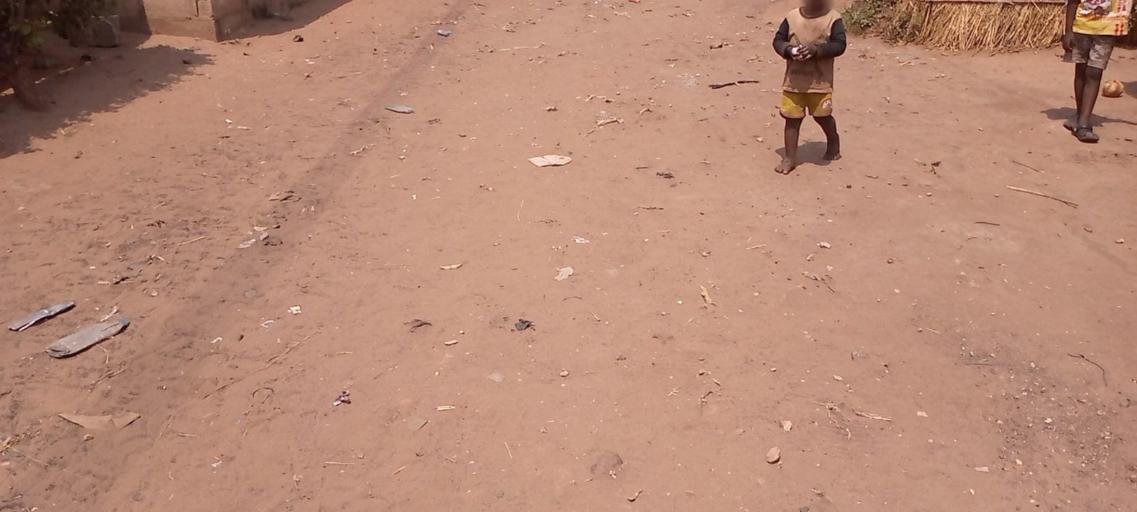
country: ZM
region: Lusaka
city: Lusaka
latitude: -15.4008
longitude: 28.3485
